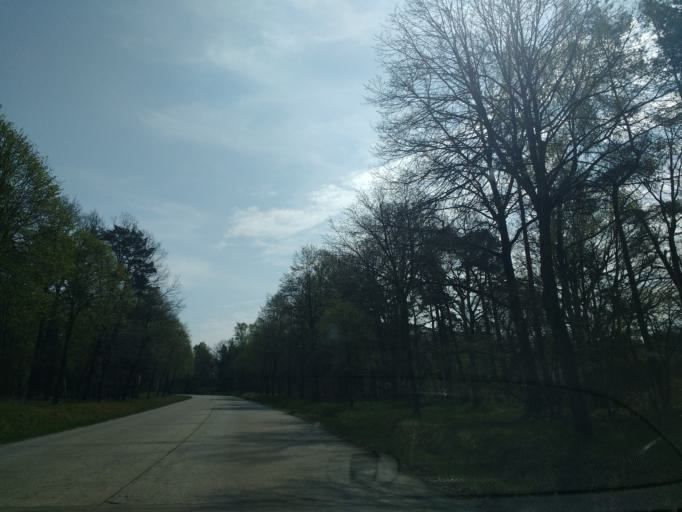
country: DE
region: North Rhine-Westphalia
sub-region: Regierungsbezirk Detmold
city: Hovelhof
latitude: 51.8269
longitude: 8.7095
